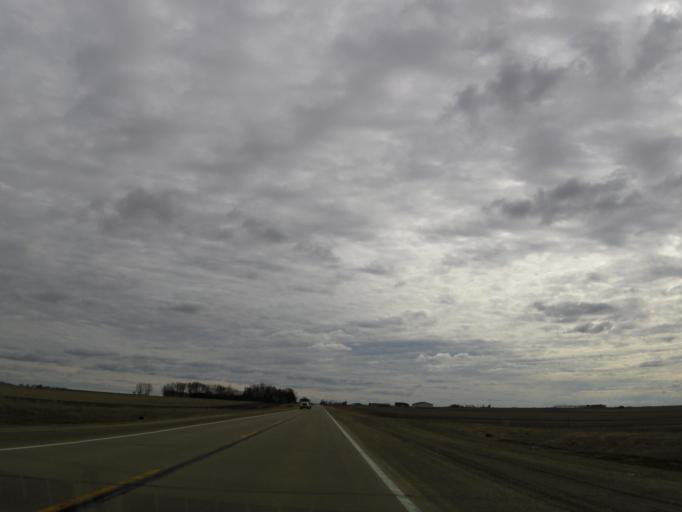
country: US
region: Iowa
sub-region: Howard County
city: Cresco
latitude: 43.4269
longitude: -92.2985
